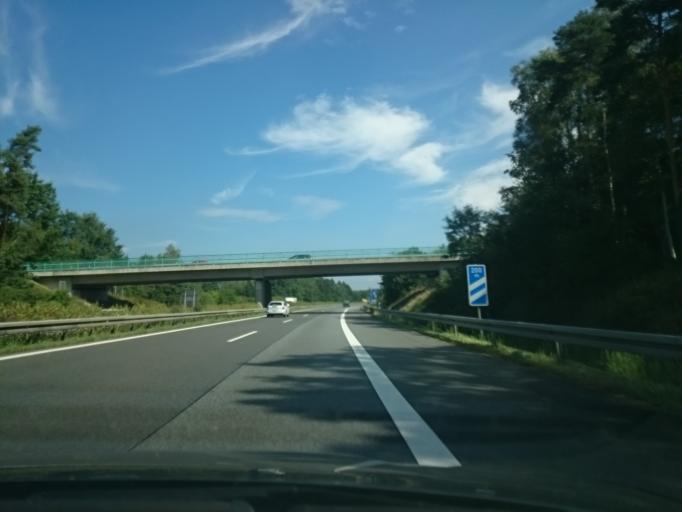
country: DE
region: Brandenburg
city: Schipkau
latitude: 51.5541
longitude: 13.9139
